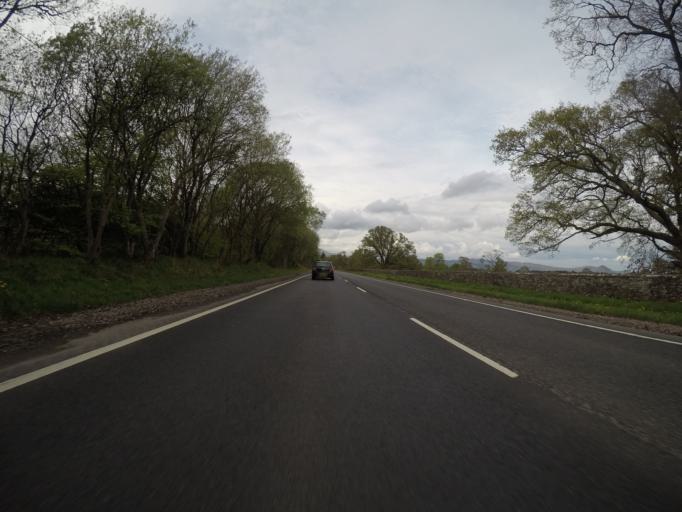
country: GB
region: Scotland
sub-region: West Dunbartonshire
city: Balloch
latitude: 56.0528
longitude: -4.6464
